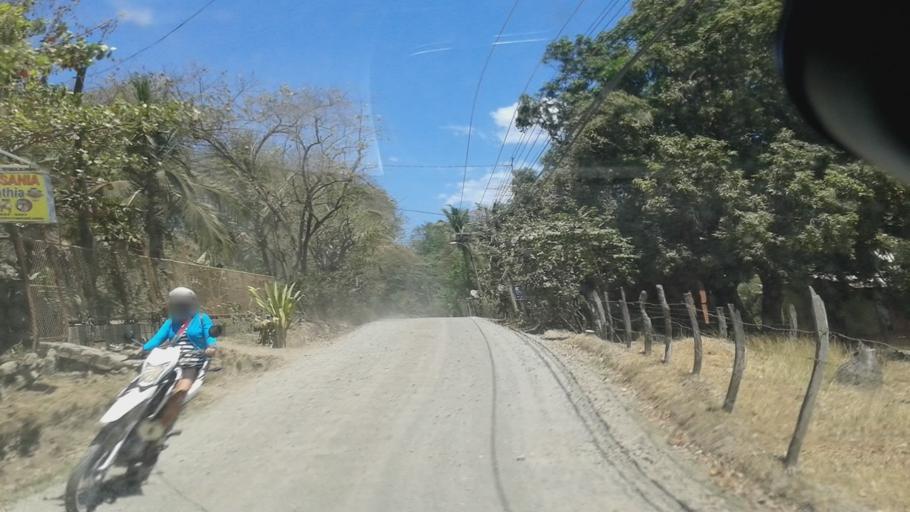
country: CR
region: Guanacaste
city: Samara
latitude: 9.9958
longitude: -85.7001
